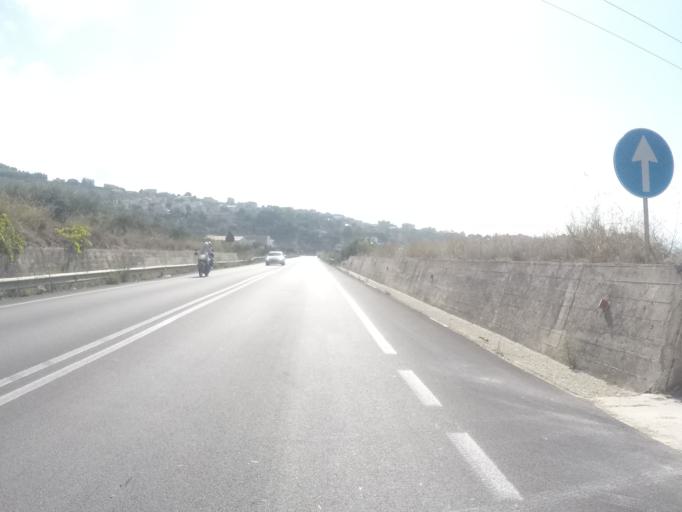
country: IT
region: Sicily
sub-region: Agrigento
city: Sciacca
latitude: 37.5158
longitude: 13.0896
